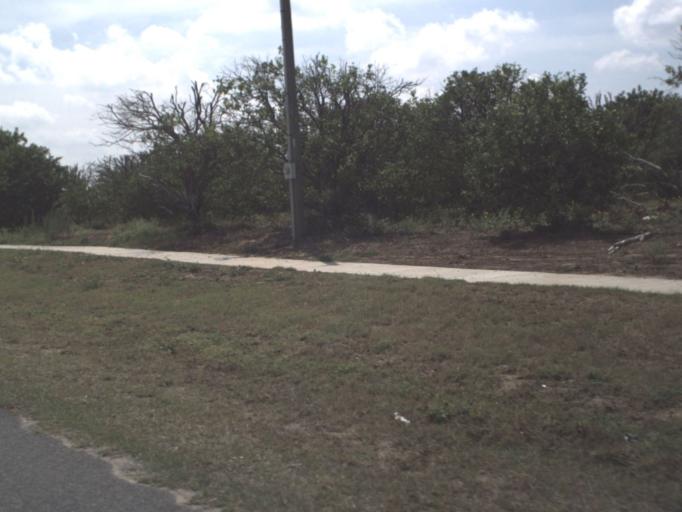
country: US
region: Florida
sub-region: Lake County
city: Tavares
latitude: 28.7745
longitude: -81.7488
